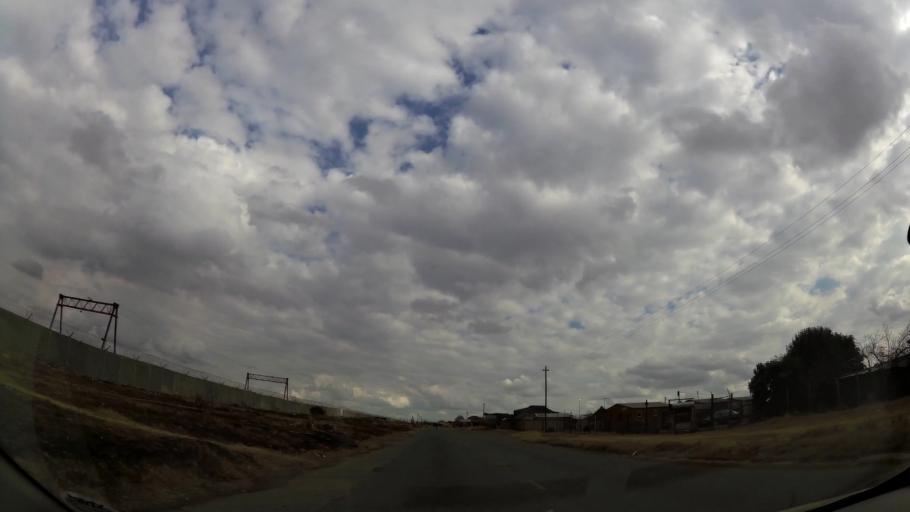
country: ZA
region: Orange Free State
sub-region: Fezile Dabi District Municipality
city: Sasolburg
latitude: -26.8605
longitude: 27.8593
